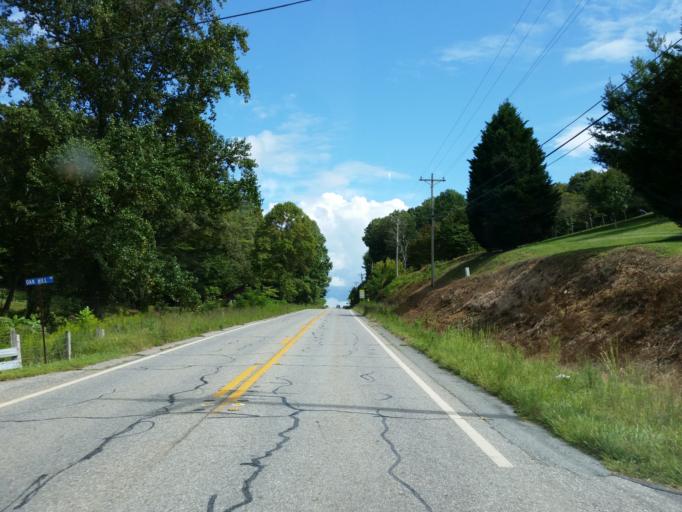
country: US
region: Georgia
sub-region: Fannin County
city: Blue Ridge
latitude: 34.8832
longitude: -84.2530
